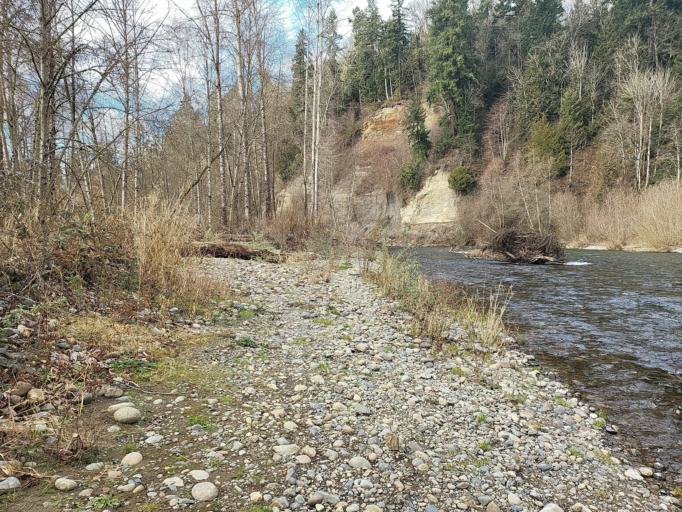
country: US
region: Washington
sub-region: King County
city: Fairwood
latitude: 47.4706
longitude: -122.1528
